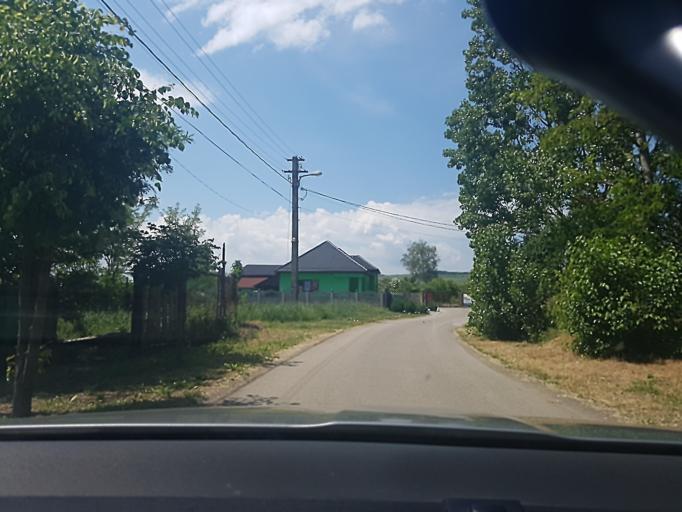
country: RO
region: Hunedoara
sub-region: Comuna Calan
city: Calan
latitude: 45.7408
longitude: 23.0052
